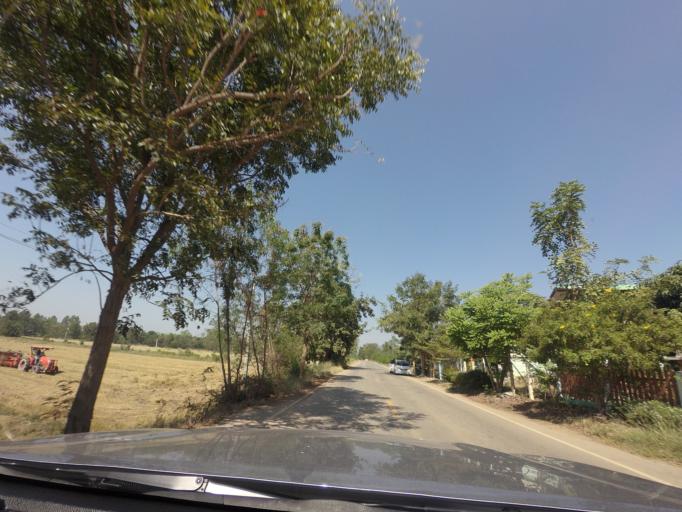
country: TH
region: Sukhothai
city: Si Samrong
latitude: 17.1430
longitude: 99.7703
